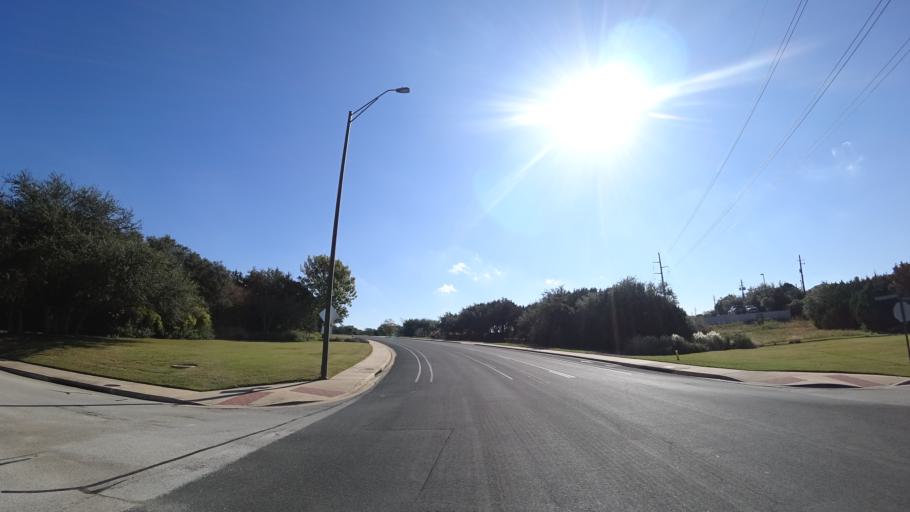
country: US
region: Texas
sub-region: Travis County
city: Hudson Bend
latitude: 30.3709
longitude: -97.8950
